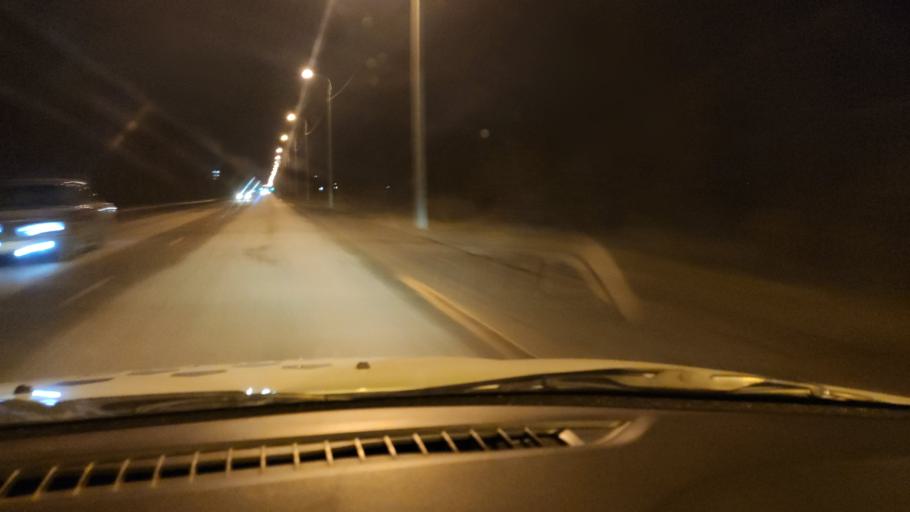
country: RU
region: Perm
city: Kondratovo
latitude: 57.9842
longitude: 56.1325
